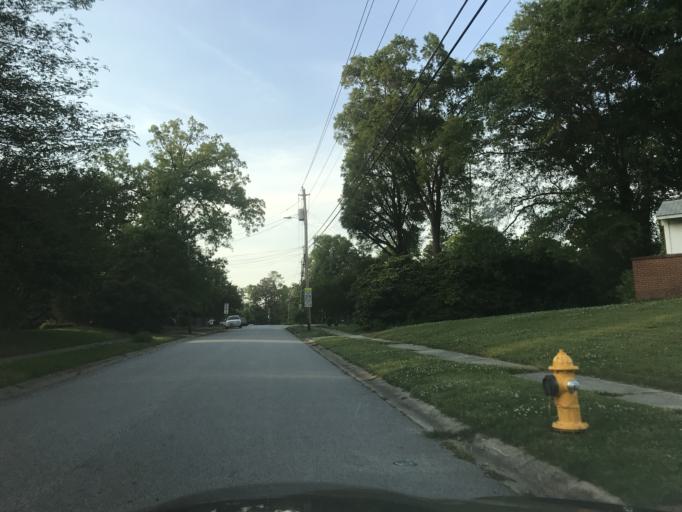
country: US
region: North Carolina
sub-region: Wake County
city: Raleigh
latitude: 35.7931
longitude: -78.6041
